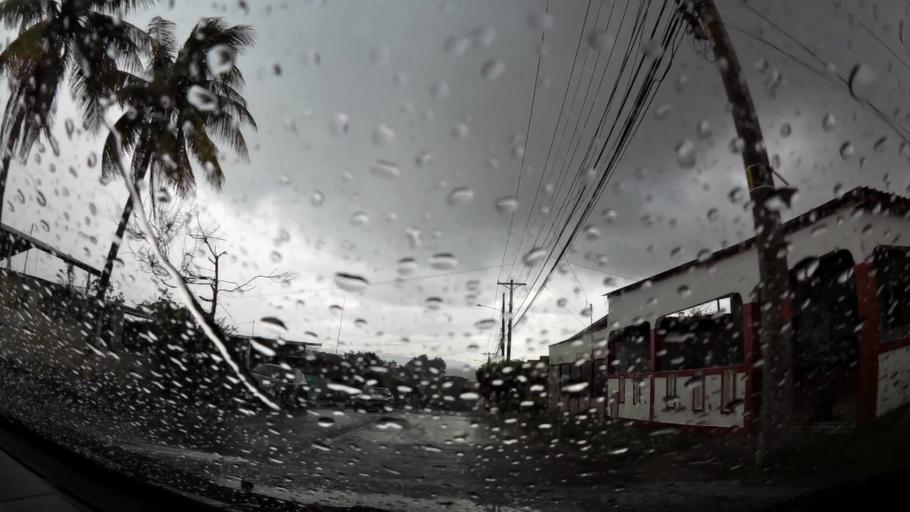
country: PA
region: Panama
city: San Miguelito
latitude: 9.0584
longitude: -79.4420
